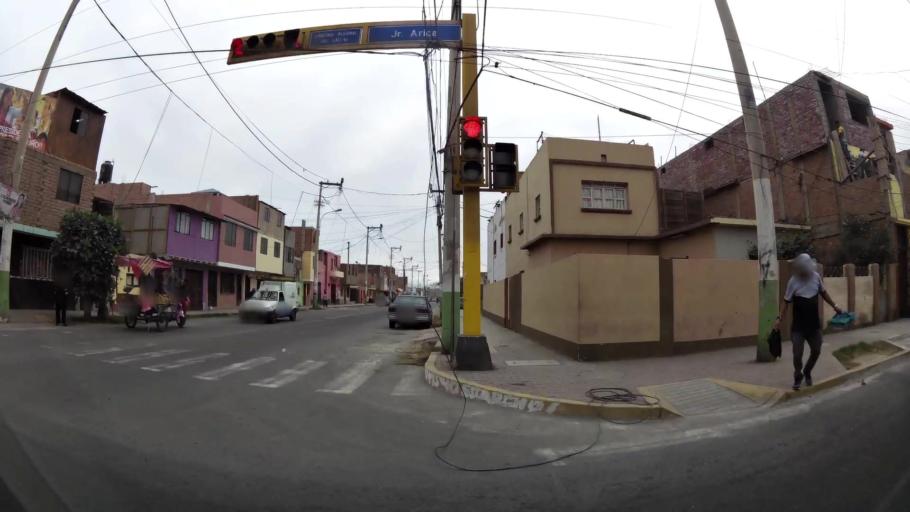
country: PE
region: Callao
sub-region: Callao
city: Callao
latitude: -12.0643
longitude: -77.1350
